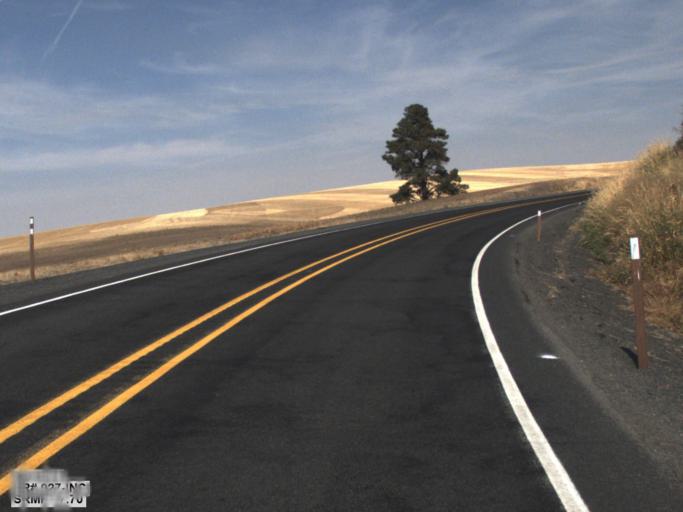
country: US
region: Washington
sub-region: Whitman County
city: Pullman
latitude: 46.9392
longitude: -117.1008
